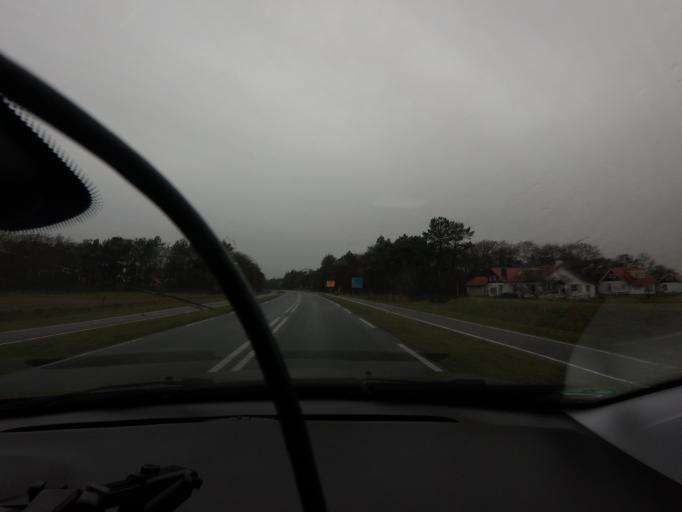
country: NL
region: North Holland
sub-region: Gemeente Texel
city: Den Burg
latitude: 53.0874
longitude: 4.7734
